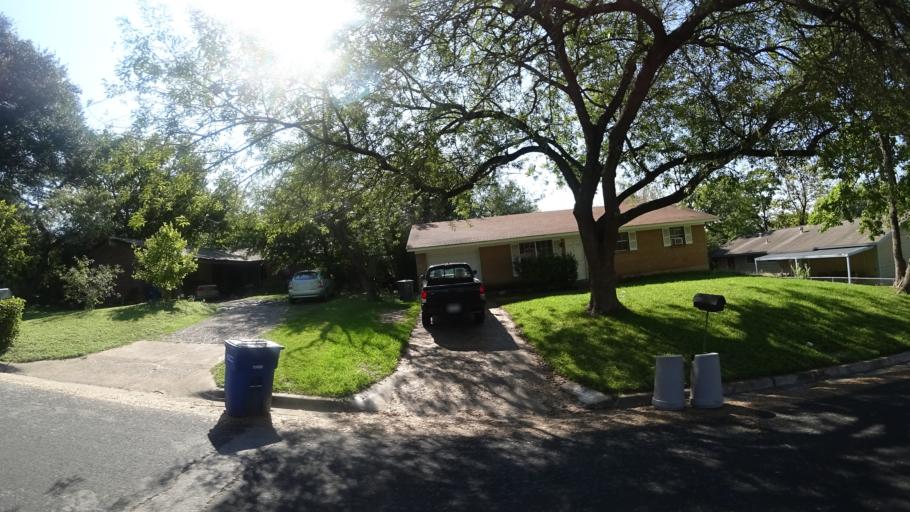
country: US
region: Texas
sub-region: Travis County
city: Austin
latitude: 30.3141
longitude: -97.6685
